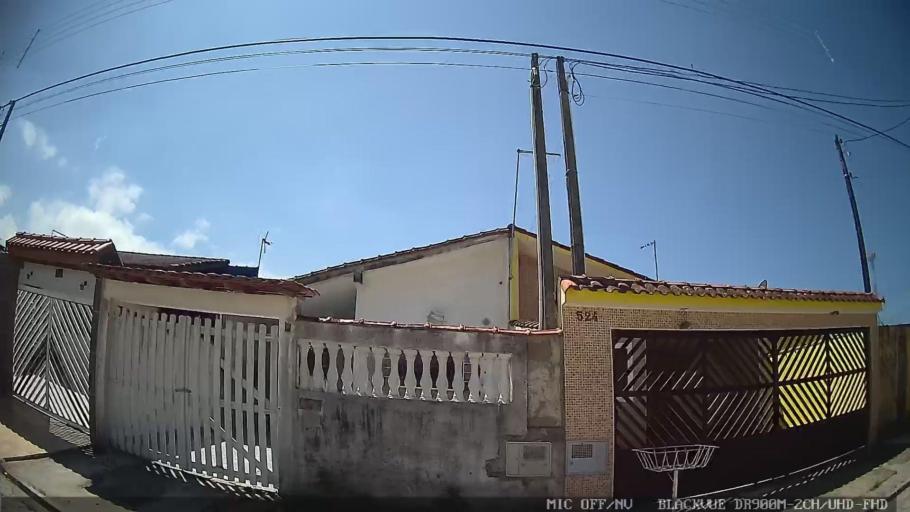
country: BR
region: Sao Paulo
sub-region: Peruibe
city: Peruibe
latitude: -24.3008
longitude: -46.9949
